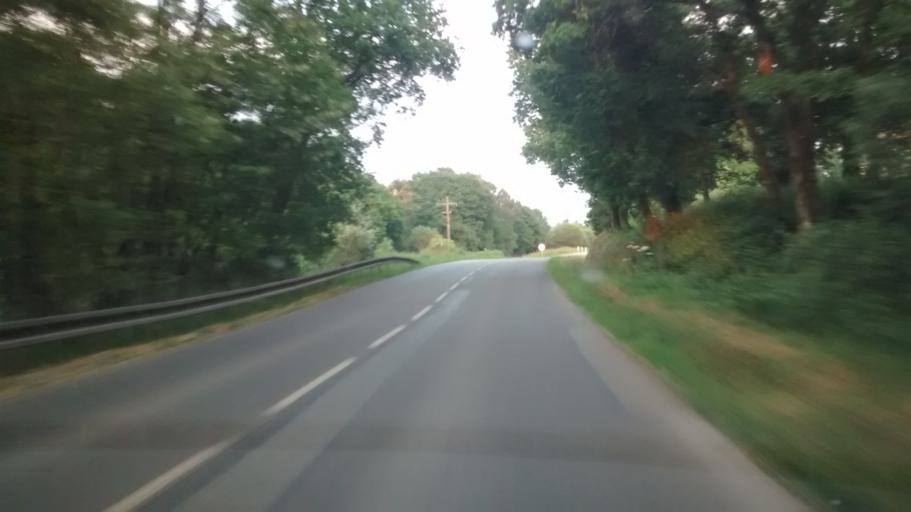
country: FR
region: Brittany
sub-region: Departement du Morbihan
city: Beignon
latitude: 47.9534
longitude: -2.1402
